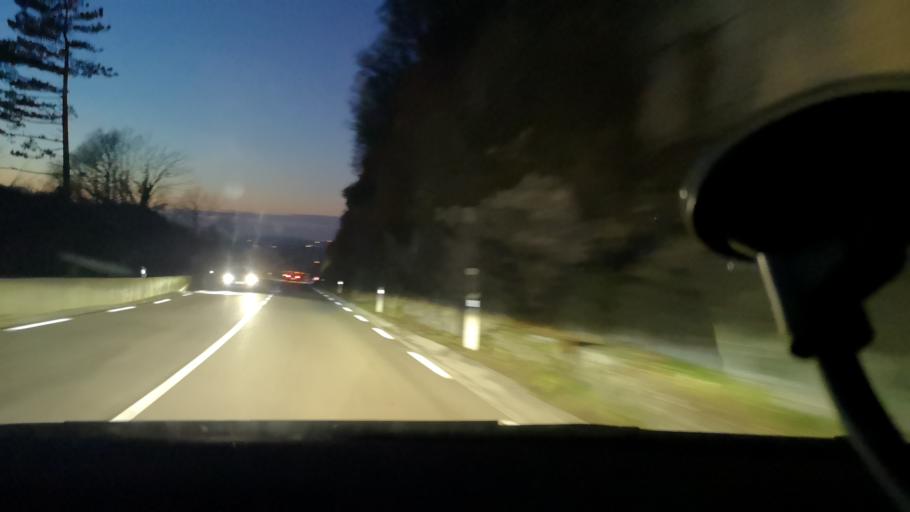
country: FR
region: Franche-Comte
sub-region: Departement du Jura
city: Poligny
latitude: 46.8201
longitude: 5.7378
